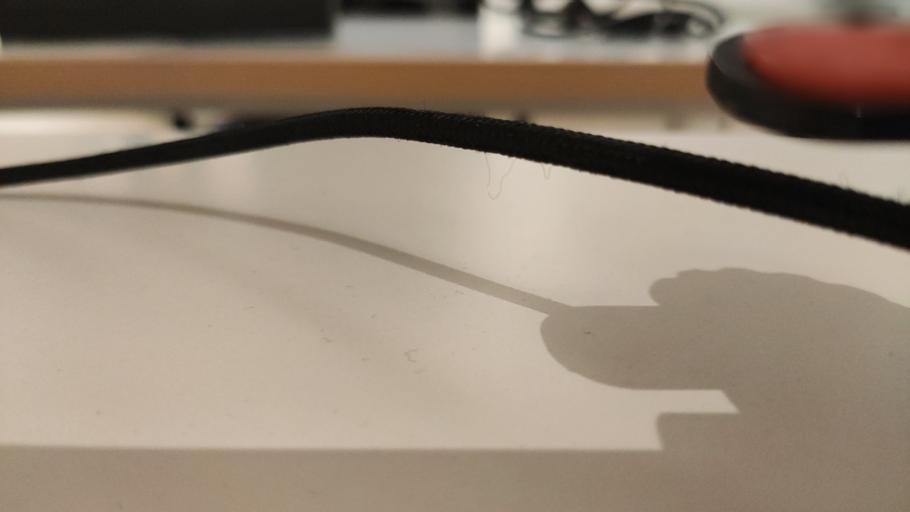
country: RU
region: Moskovskaya
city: Dorokhovo
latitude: 55.5425
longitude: 36.3826
